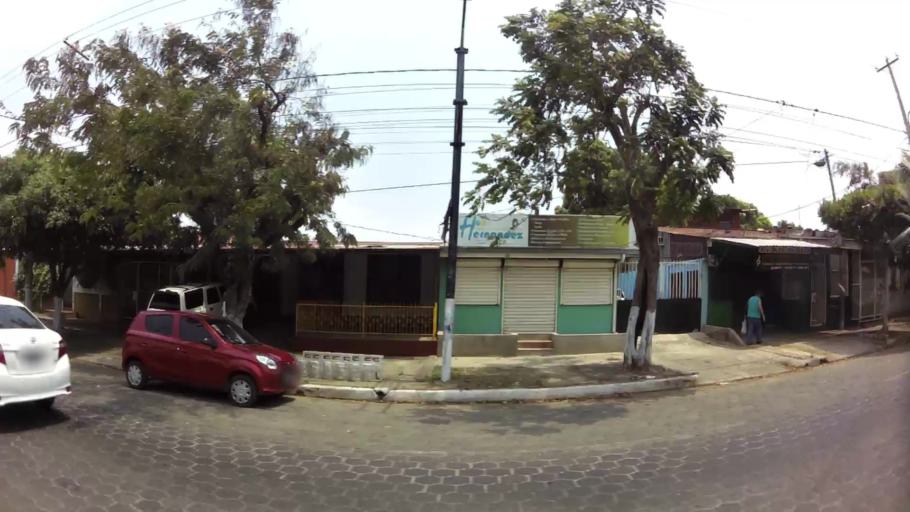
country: NI
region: Managua
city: Ciudad Sandino
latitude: 12.1450
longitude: -86.3028
